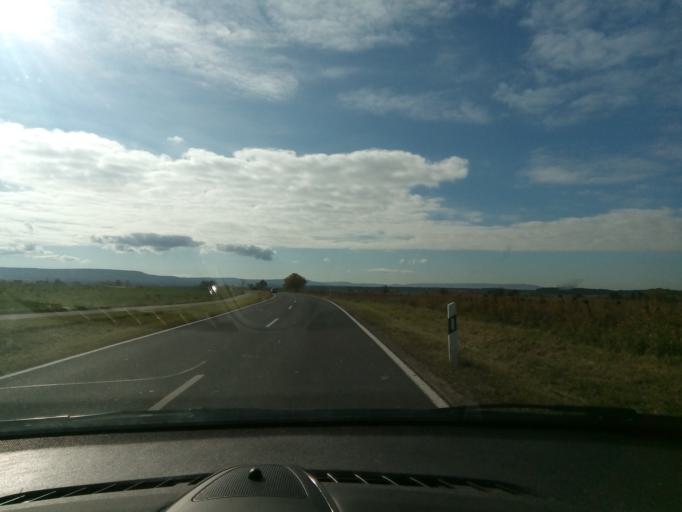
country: DE
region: Bavaria
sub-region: Regierungsbezirk Unterfranken
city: Oberschwarzach
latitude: 49.8720
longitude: 10.4021
